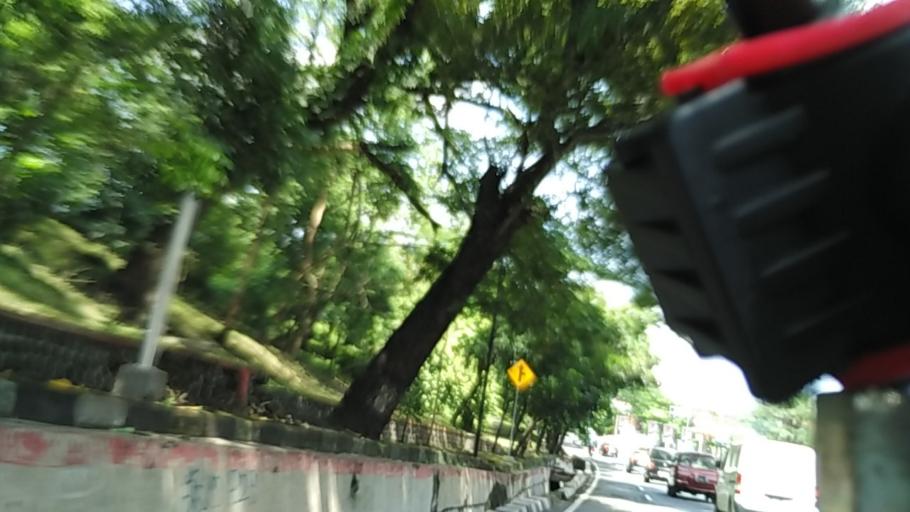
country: ID
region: Central Java
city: Semarang
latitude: -7.0016
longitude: 110.4068
